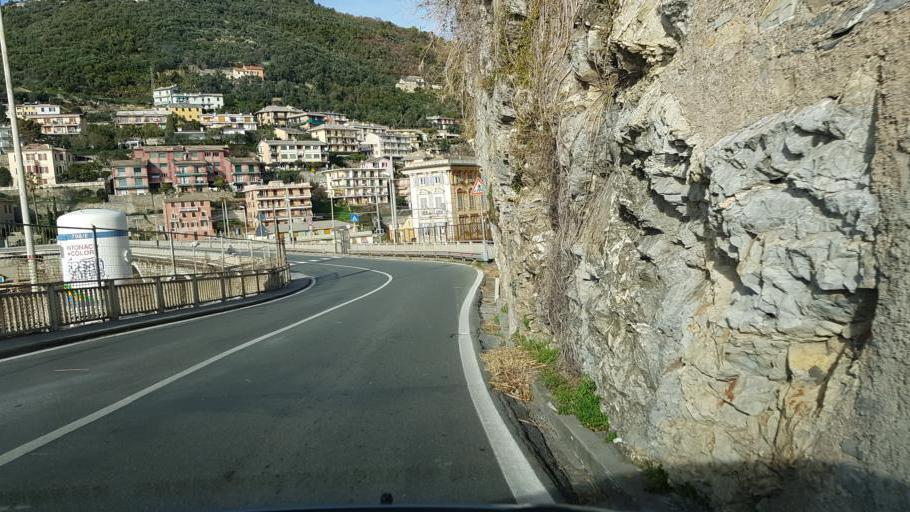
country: IT
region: Liguria
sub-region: Provincia di Genova
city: Sori
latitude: 44.3710
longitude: 9.1047
